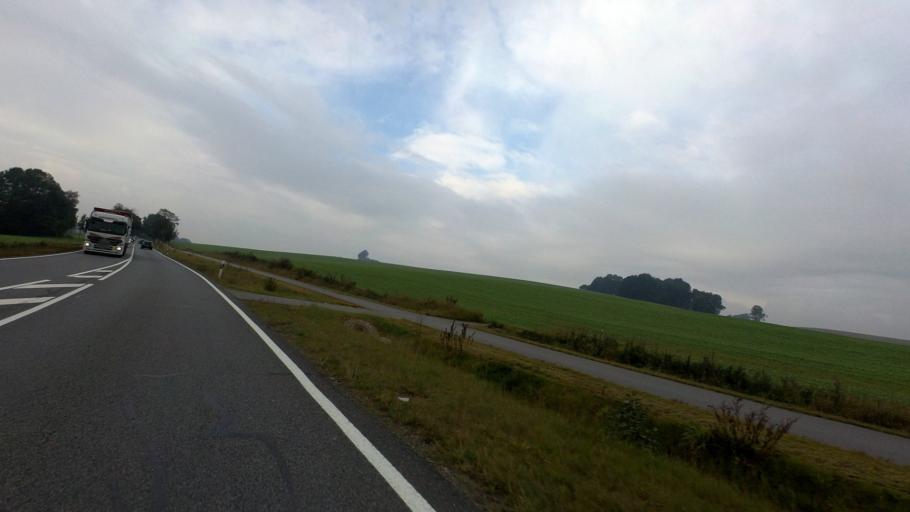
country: DE
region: Saxony
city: Bischofswerda
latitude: 51.1207
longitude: 14.1629
